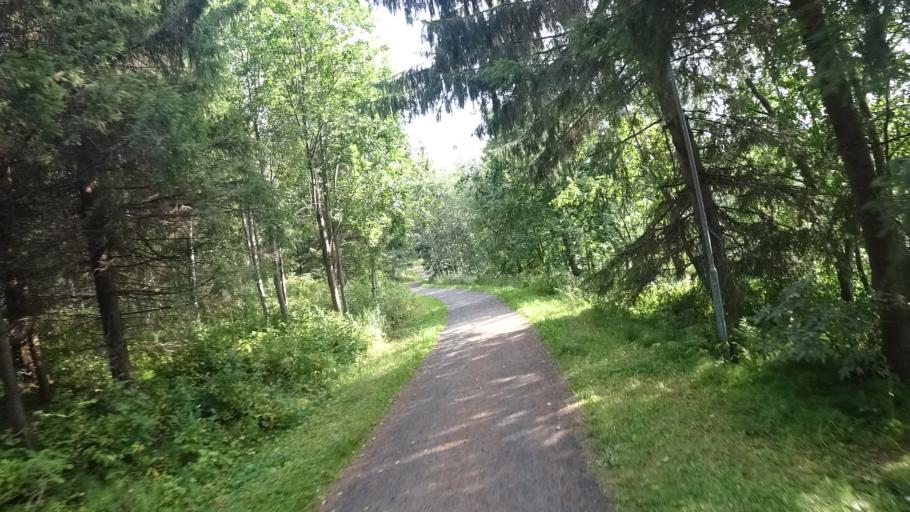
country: FI
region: North Karelia
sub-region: Joensuu
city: Ilomantsi
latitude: 62.6732
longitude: 30.9133
